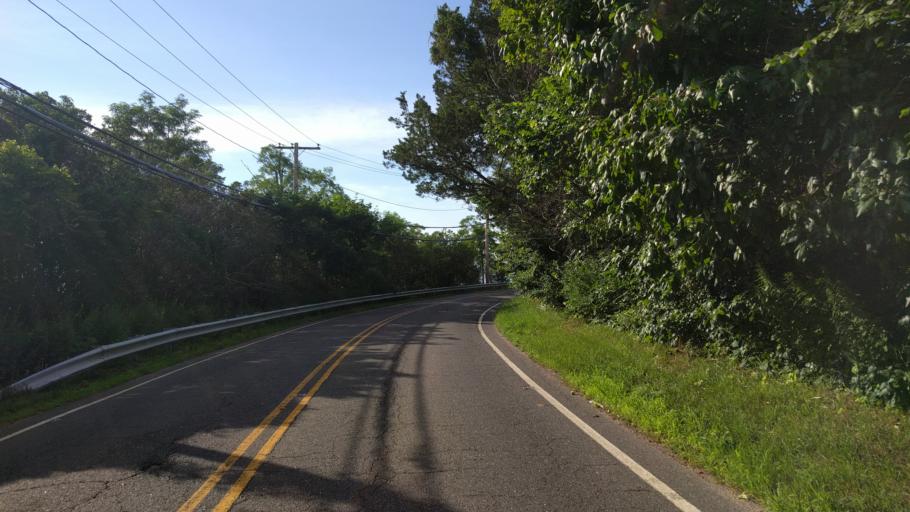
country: US
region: New York
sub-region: Nassau County
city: Oyster Bay Cove
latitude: 40.8754
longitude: -73.5043
